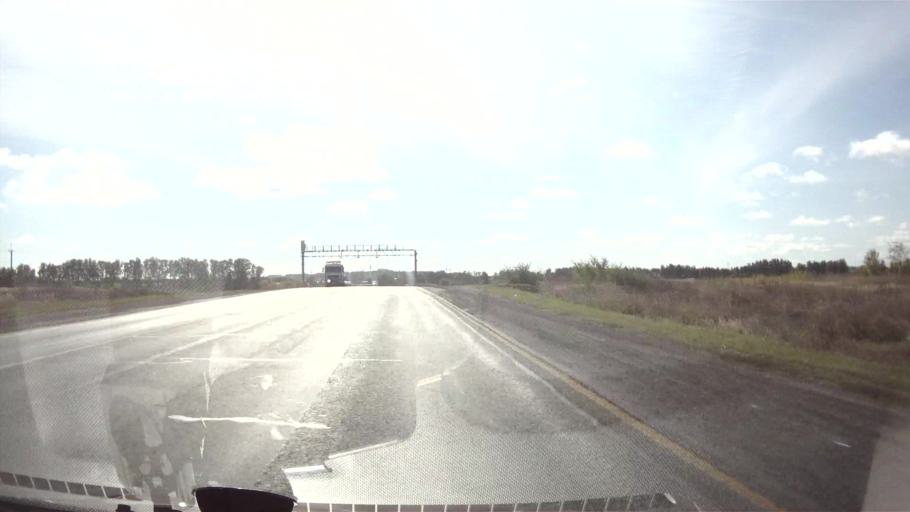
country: RU
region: Ulyanovsk
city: Isheyevka
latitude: 54.2992
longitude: 48.2460
